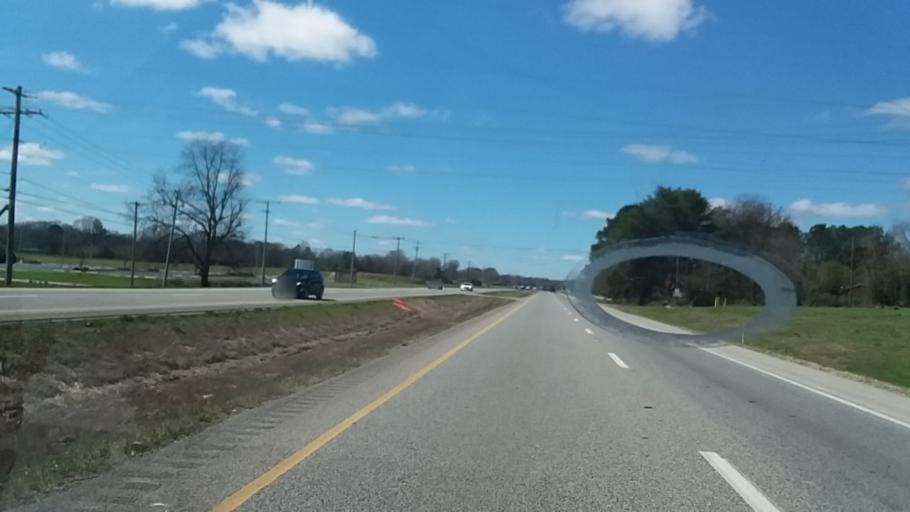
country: US
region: Alabama
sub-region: Colbert County
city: Tuscumbia
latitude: 34.7149
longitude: -87.6780
